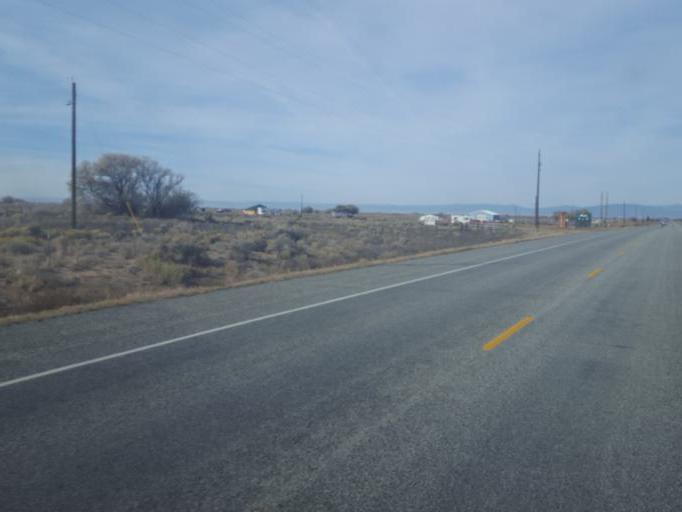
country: US
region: Colorado
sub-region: Alamosa County
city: Alamosa East
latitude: 37.4744
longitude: -105.7302
